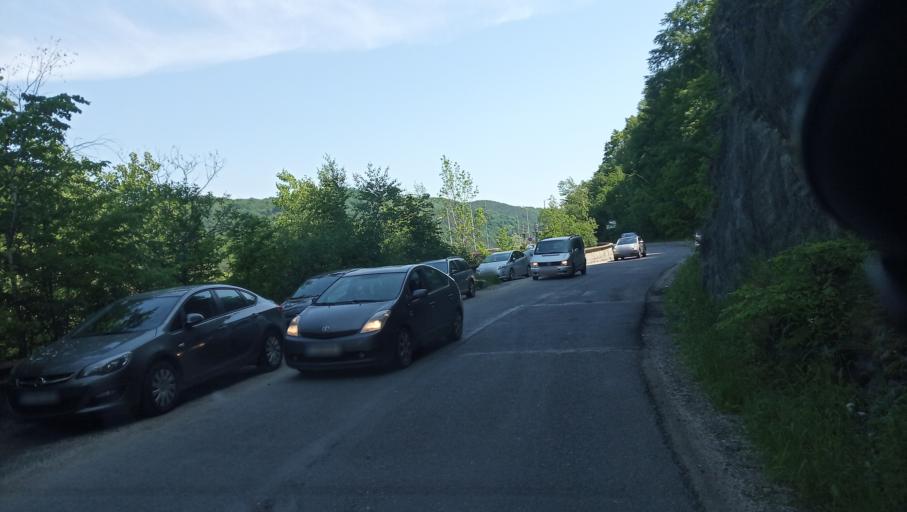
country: RO
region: Cluj
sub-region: Comuna Capusu Mare
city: Capusu Mare
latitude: 46.7257
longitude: 23.3003
